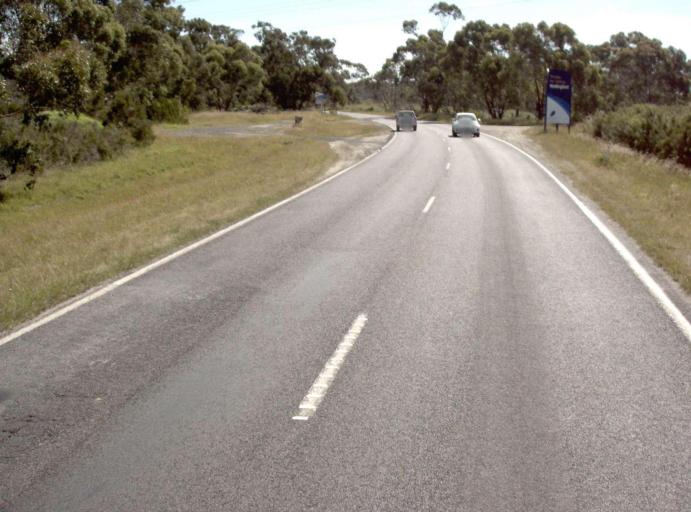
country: AU
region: Victoria
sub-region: Latrobe
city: Morwell
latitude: -38.6362
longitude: 146.5271
